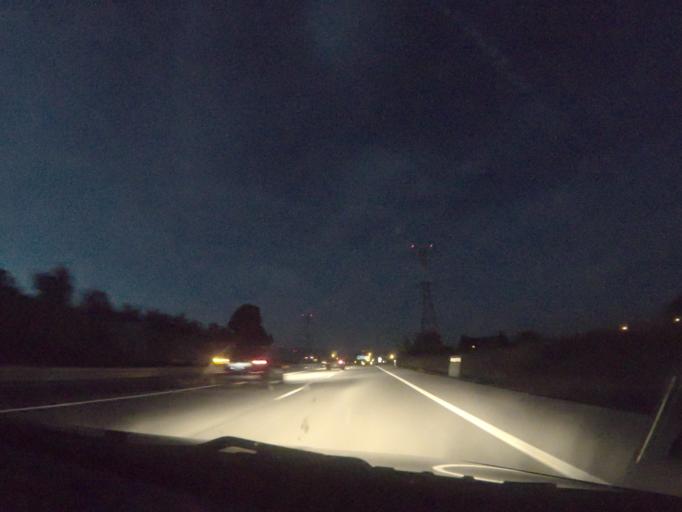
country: PT
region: Guarda
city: Alcains
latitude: 39.9800
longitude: -7.4590
